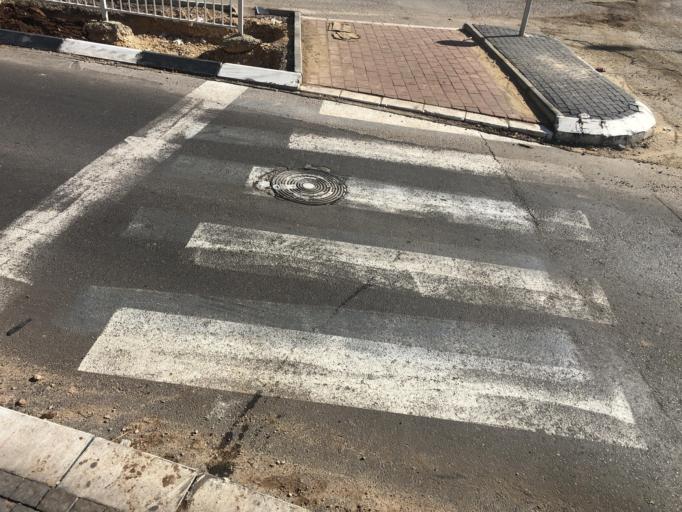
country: IL
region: Jerusalem
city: Modiin Ilit
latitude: 31.9294
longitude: 35.0457
